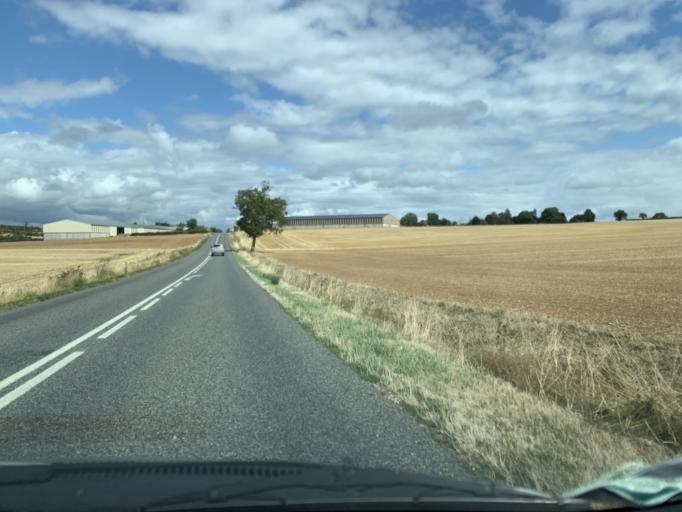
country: FR
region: Bourgogne
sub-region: Departement de la Nievre
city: Varzy
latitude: 47.3712
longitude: 3.4213
